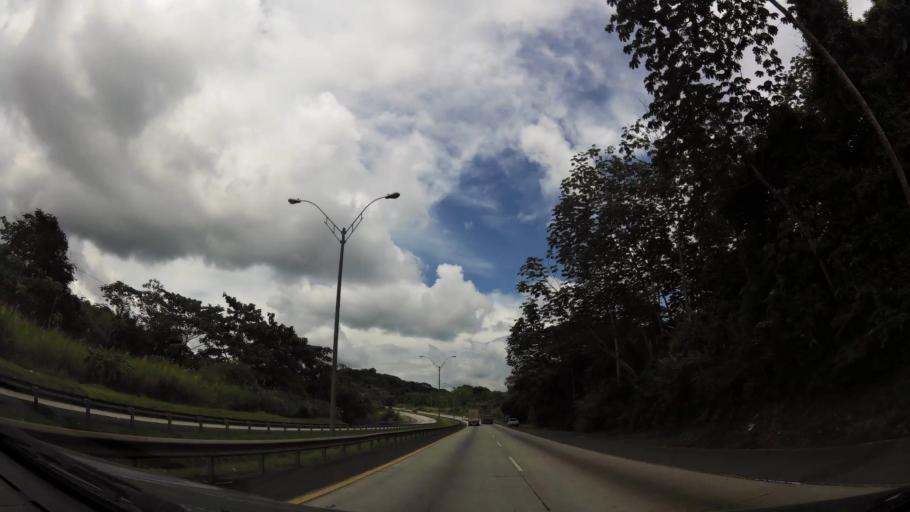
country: PA
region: Panama
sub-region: Distrito Arraijan
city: Arraijan
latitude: 8.9882
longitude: -79.6481
